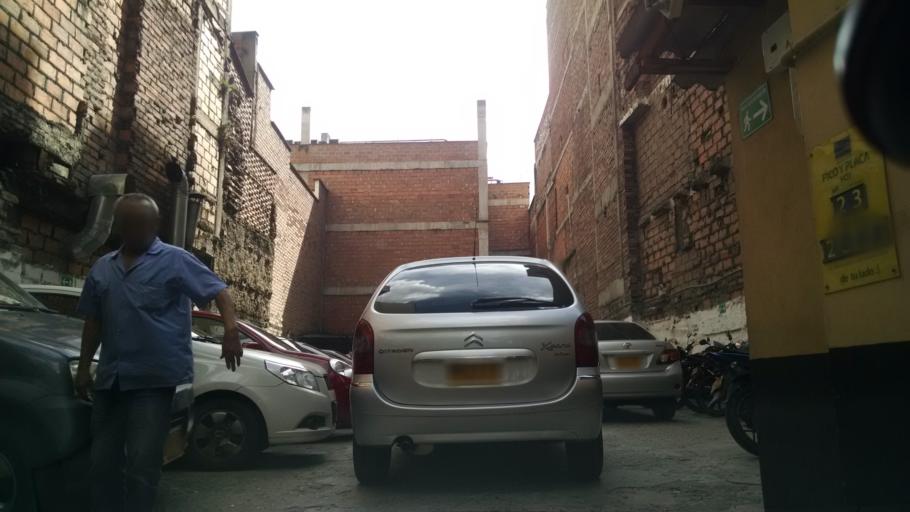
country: CO
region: Antioquia
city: Medellin
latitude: 6.2488
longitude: -75.5640
